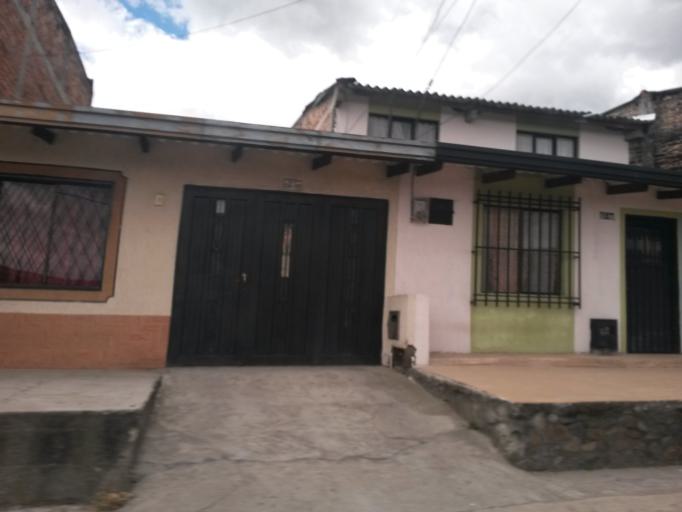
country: CO
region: Cauca
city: Popayan
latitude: 2.4488
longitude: -76.6305
